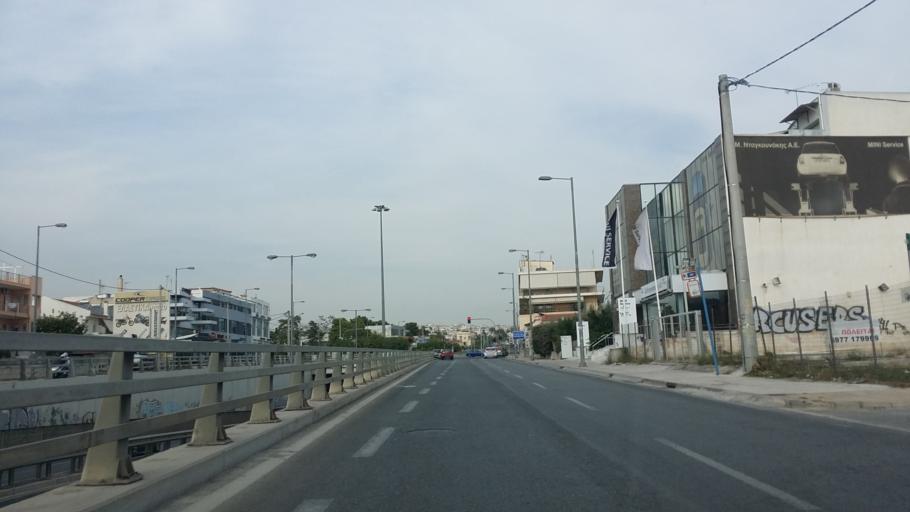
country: GR
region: Attica
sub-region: Nomarchia Athinas
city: Filothei
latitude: 38.0393
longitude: 23.7757
